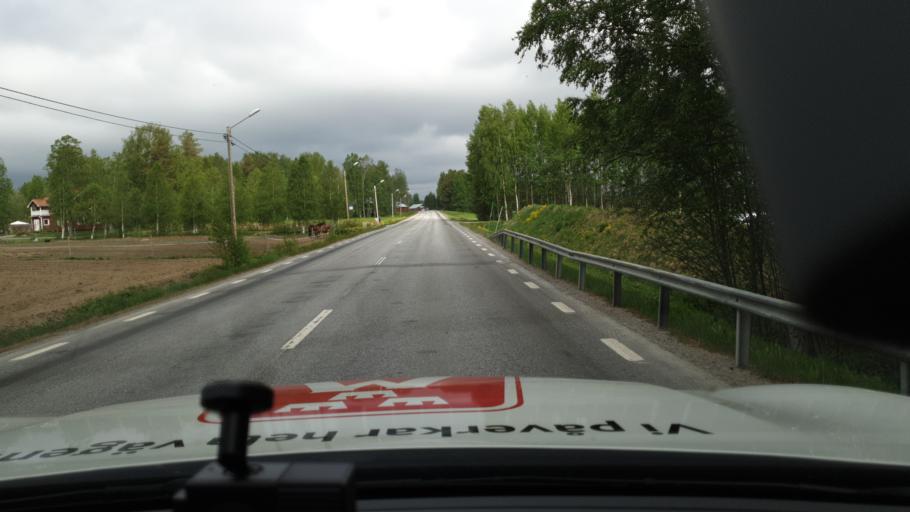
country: SE
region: Vaesterbotten
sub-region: Umea Kommun
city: Roback
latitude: 63.9299
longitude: 20.1776
